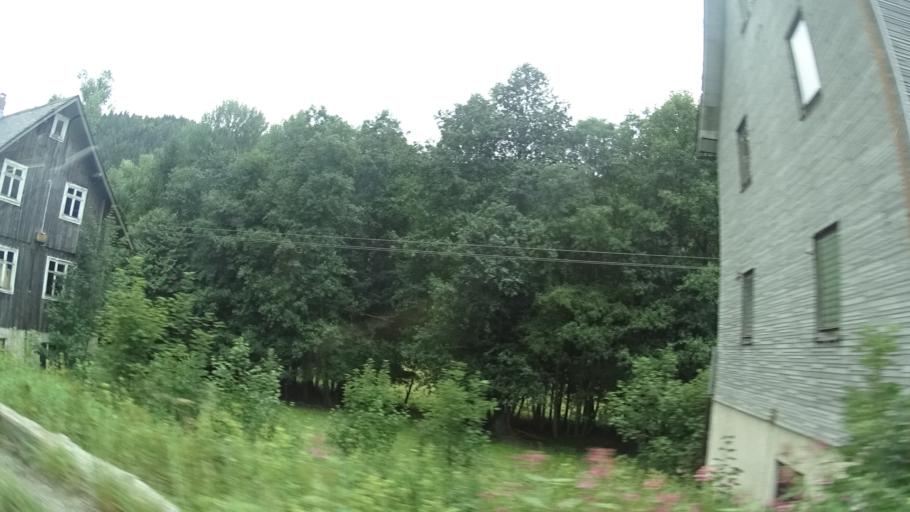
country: DE
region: Bavaria
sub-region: Upper Franconia
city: Tettau
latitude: 50.4387
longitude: 11.2658
